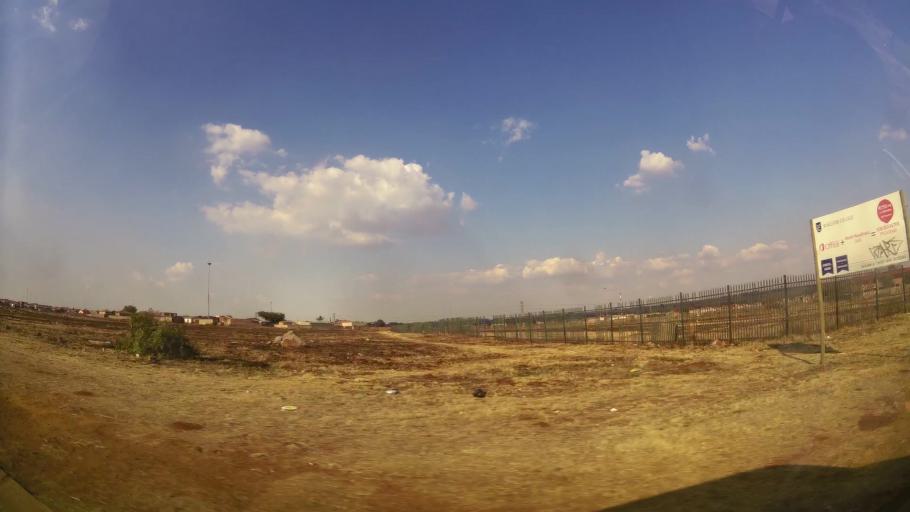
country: ZA
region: Gauteng
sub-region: Ekurhuleni Metropolitan Municipality
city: Germiston
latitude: -26.3677
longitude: 28.2190
